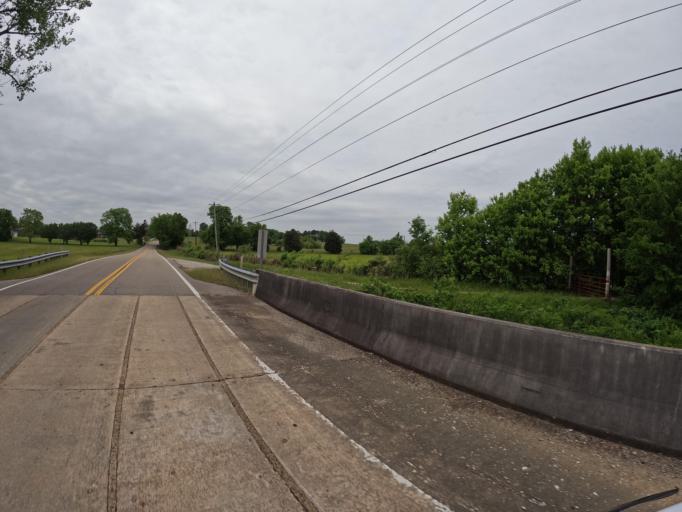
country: US
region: Mississippi
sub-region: Lee County
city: Tupelo
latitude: 34.2908
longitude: -88.7642
